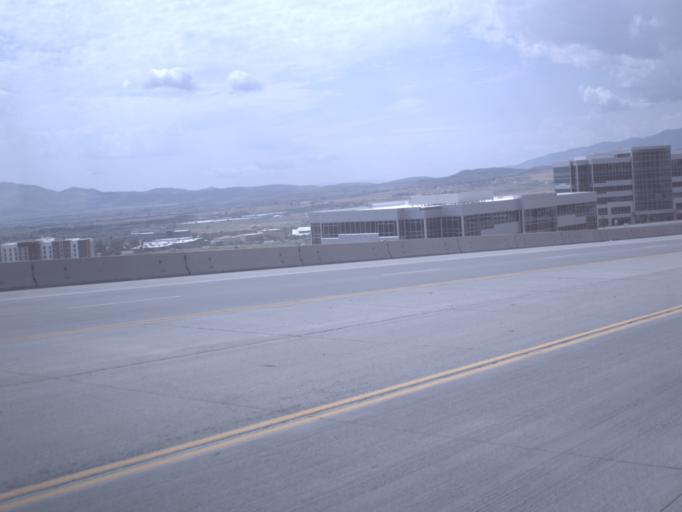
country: US
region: Utah
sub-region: Utah County
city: Lehi
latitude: 40.4319
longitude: -111.8776
